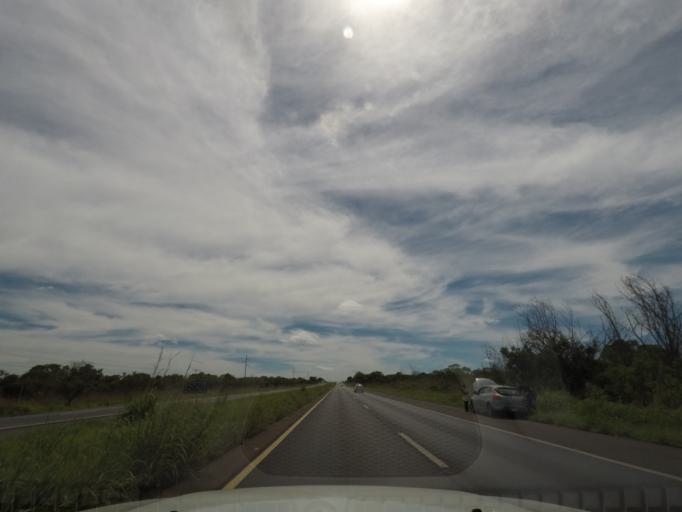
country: BR
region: Goias
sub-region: Planaltina
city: Planaltina
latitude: -15.5960
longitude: -47.6454
